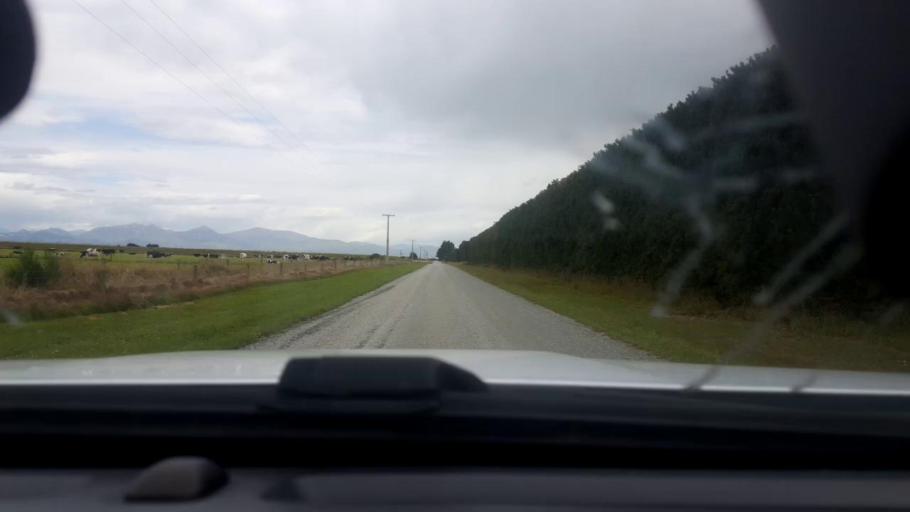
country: NZ
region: Canterbury
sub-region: Timaru District
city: Pleasant Point
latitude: -44.1483
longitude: 171.3903
